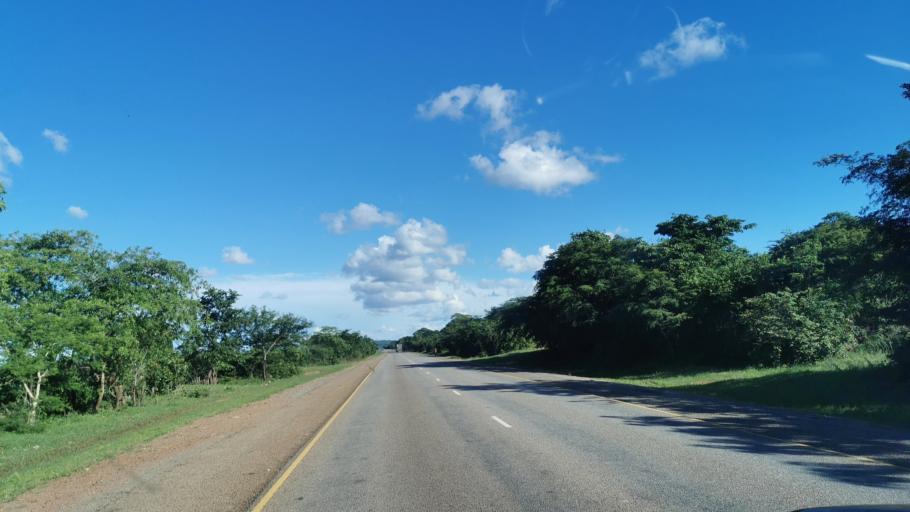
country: TZ
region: Geita
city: Masumbwe
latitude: -3.7202
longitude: 32.2971
